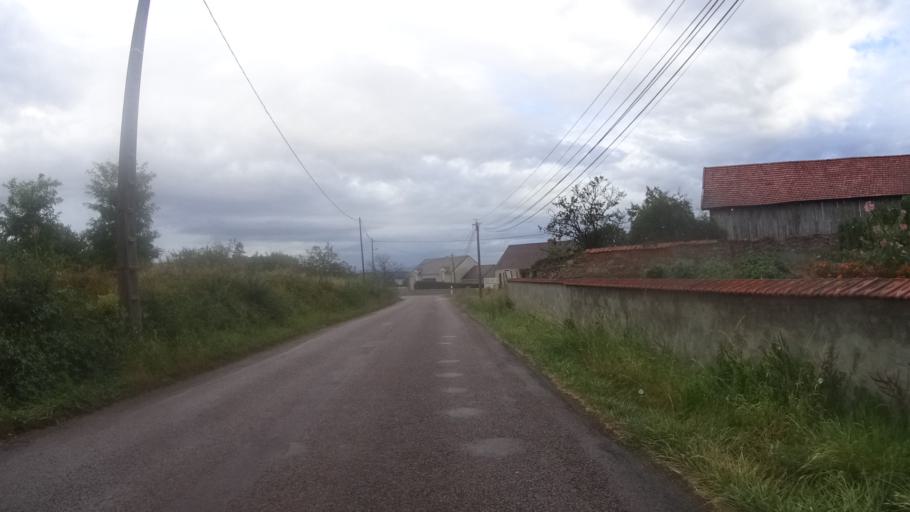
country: FR
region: Bourgogne
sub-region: Departement de Saone-et-Loire
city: Gergy
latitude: 46.9506
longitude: 4.9469
